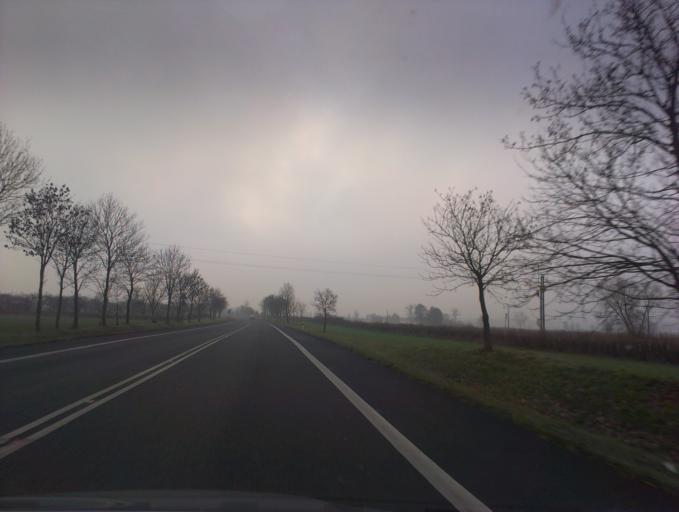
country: PL
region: Greater Poland Voivodeship
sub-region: Powiat chodzieski
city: Budzyn
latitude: 52.8888
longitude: 16.9697
